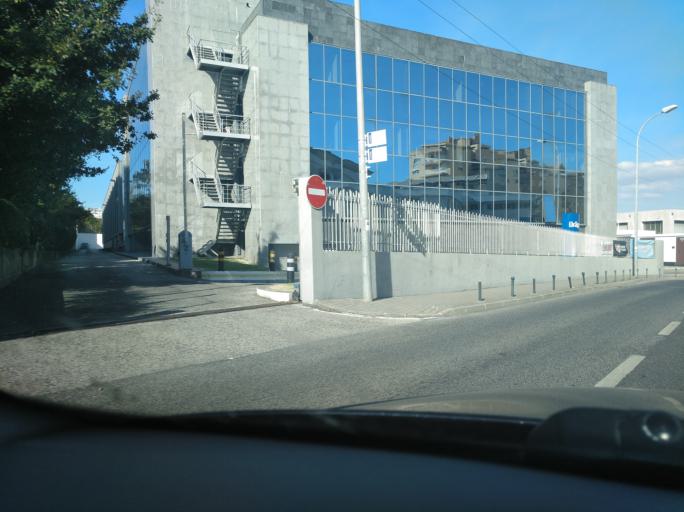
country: PT
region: Lisbon
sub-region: Oeiras
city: Linda-a-Velha
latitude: 38.7208
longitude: -9.2334
